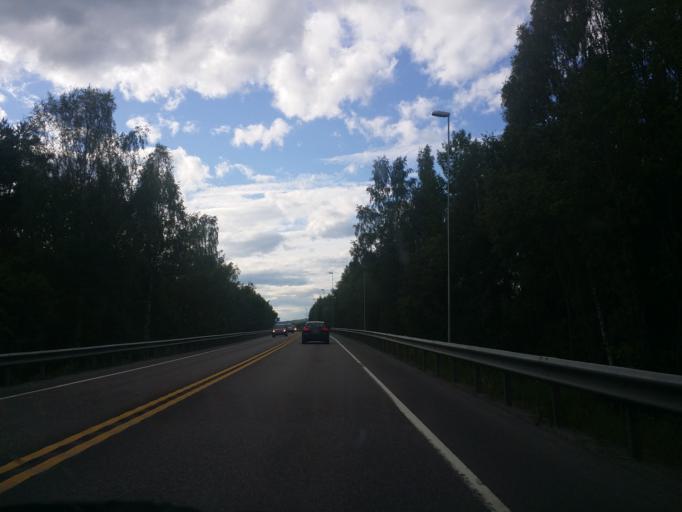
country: NO
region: Hedmark
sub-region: Hamar
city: Hamar
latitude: 60.7953
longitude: 11.1217
